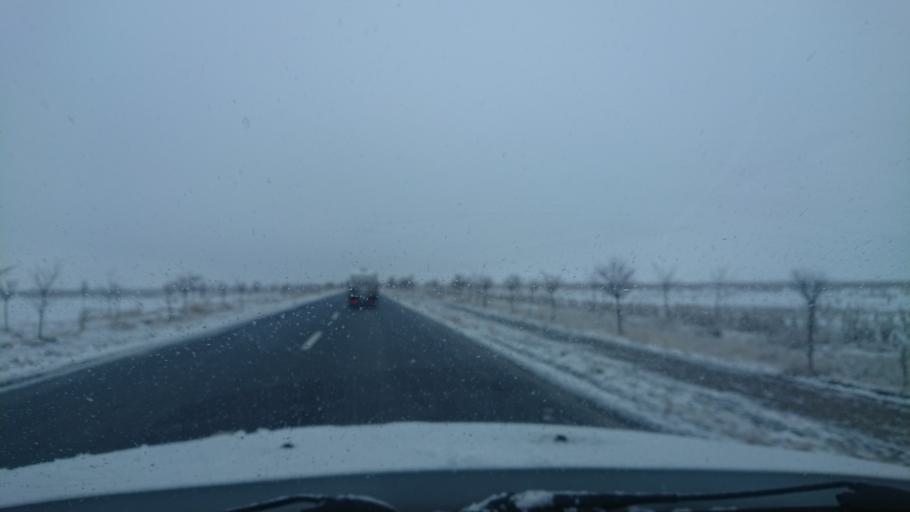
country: TR
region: Aksaray
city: Yesilova
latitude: 38.3146
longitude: 33.7537
